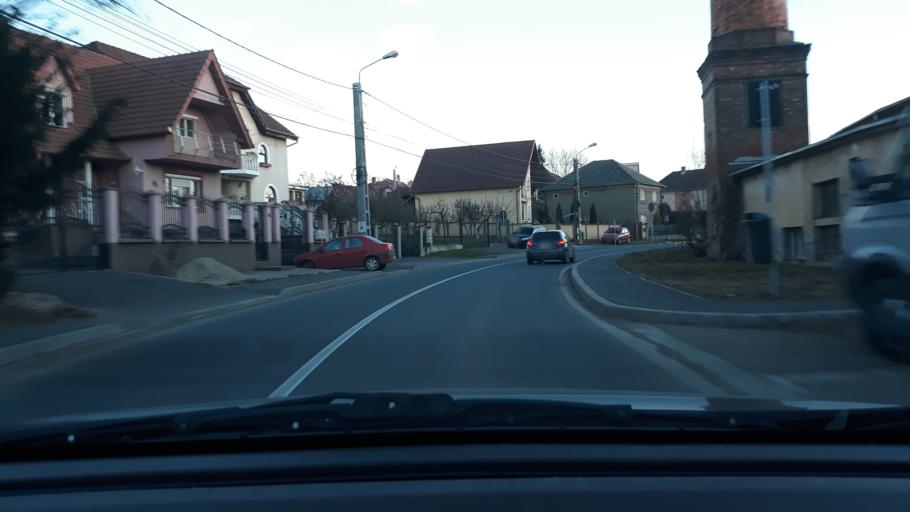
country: RO
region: Bihor
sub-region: Comuna Biharea
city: Oradea
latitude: 47.0819
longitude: 21.9280
